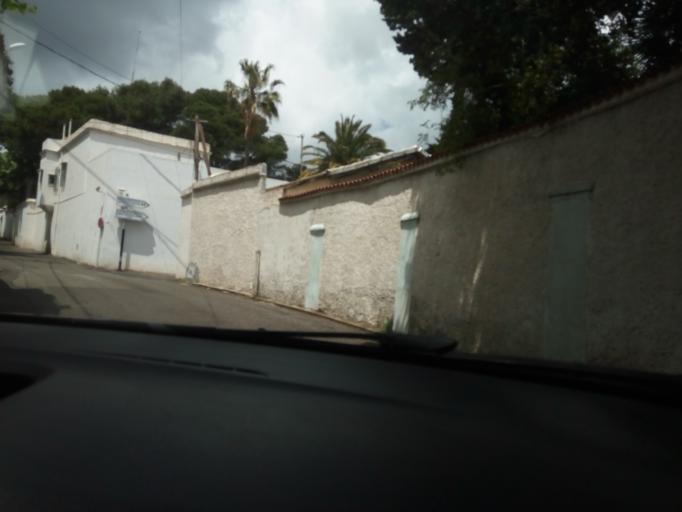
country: DZ
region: Alger
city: Algiers
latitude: 36.7648
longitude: 3.0337
